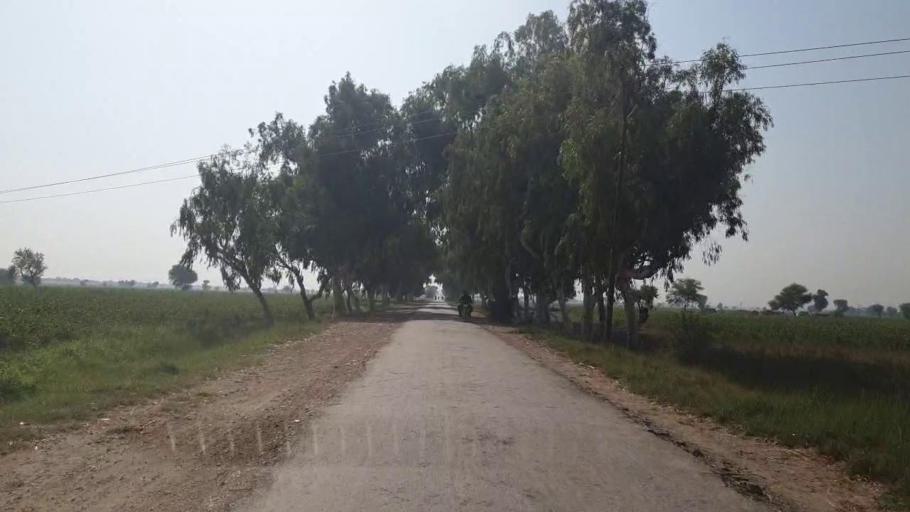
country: PK
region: Sindh
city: Shahdadpur
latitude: 25.9360
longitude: 68.7286
